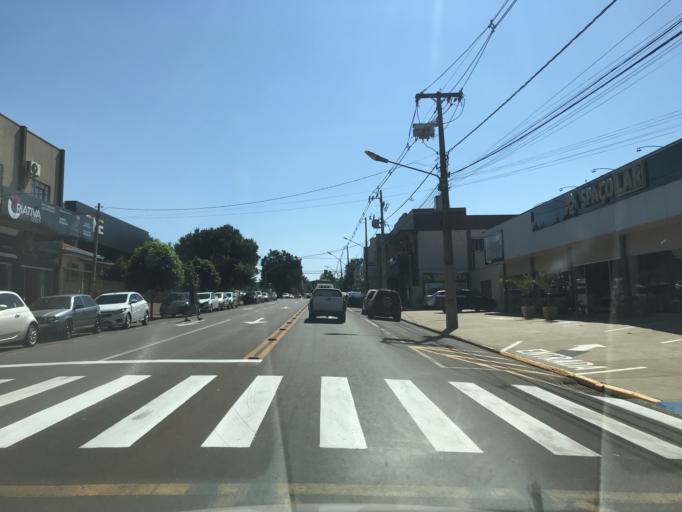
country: BR
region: Parana
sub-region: Toledo
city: Toledo
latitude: -24.7310
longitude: -53.7361
